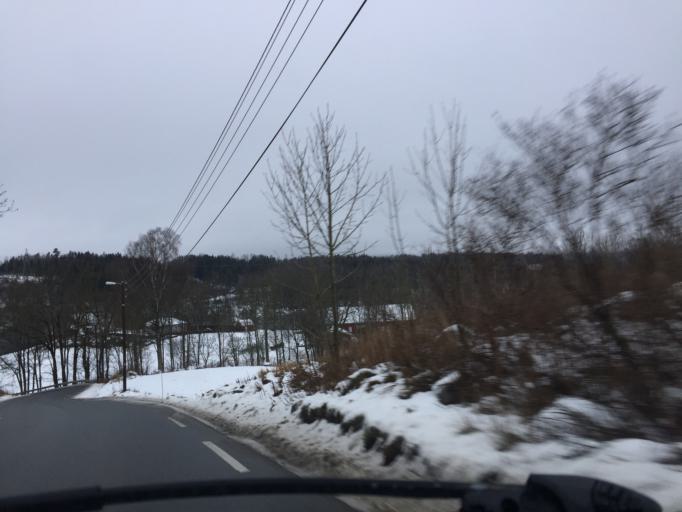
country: NO
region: Akershus
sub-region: As
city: As
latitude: 59.7021
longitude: 10.7457
